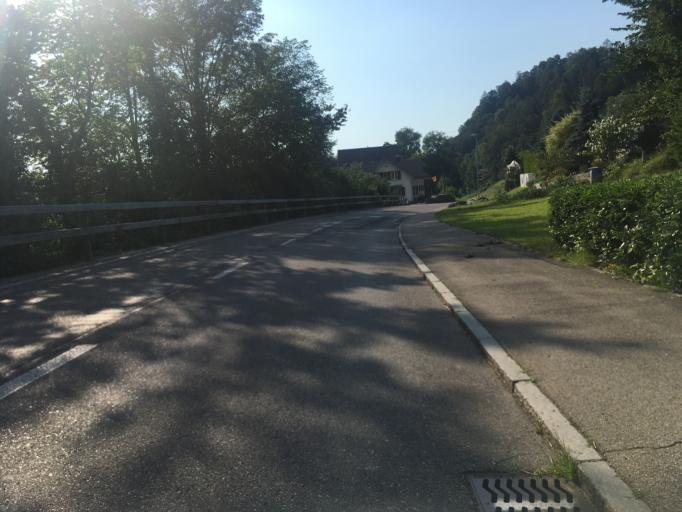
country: CH
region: Bern
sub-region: Emmental District
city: Lutzelfluh
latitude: 47.0089
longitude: 7.6840
